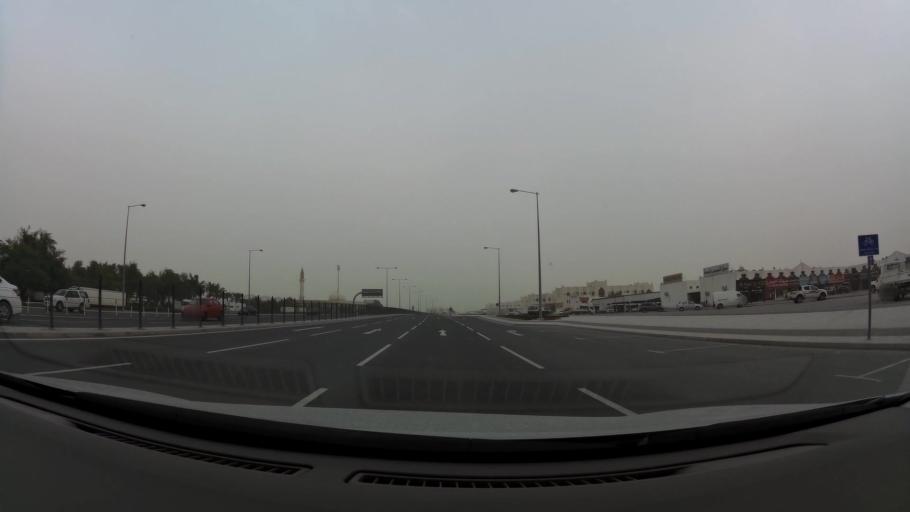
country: QA
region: Baladiyat ad Dawhah
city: Doha
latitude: 25.2477
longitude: 51.4726
